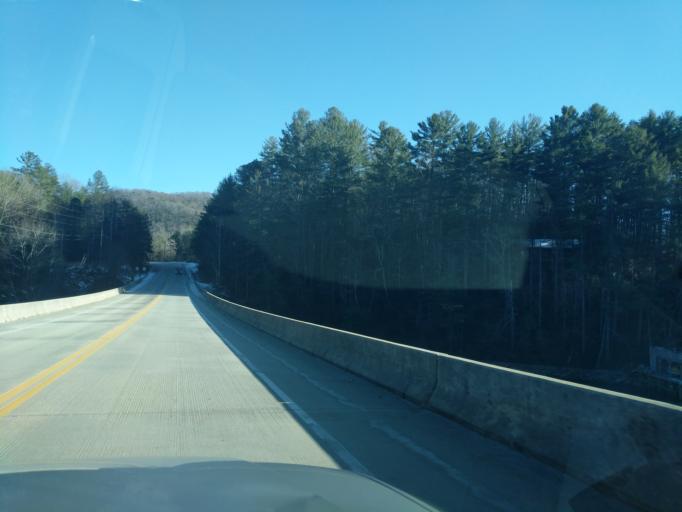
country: US
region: Georgia
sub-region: Rabun County
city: Clayton
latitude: 34.8686
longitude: -83.5403
